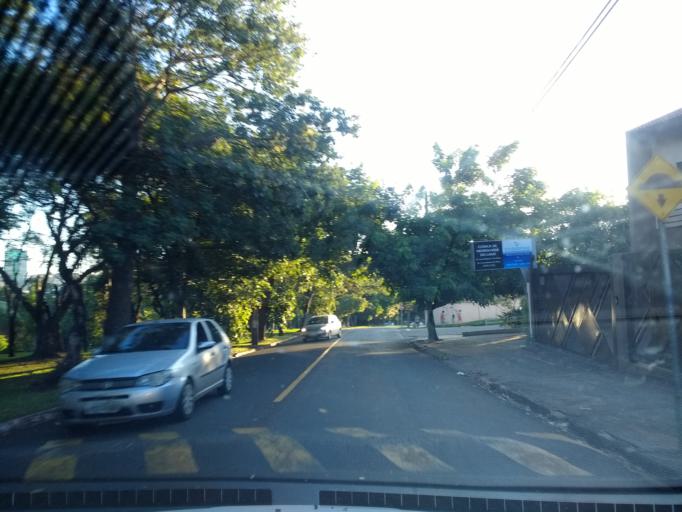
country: BR
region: Parana
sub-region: Londrina
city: Londrina
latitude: -23.3315
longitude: -51.1592
